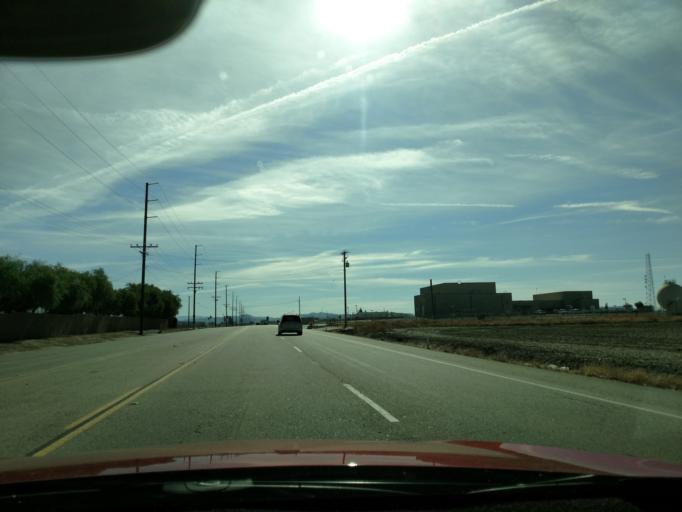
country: US
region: California
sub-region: Riverside County
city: San Jacinto
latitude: 33.8009
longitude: -117.0069
